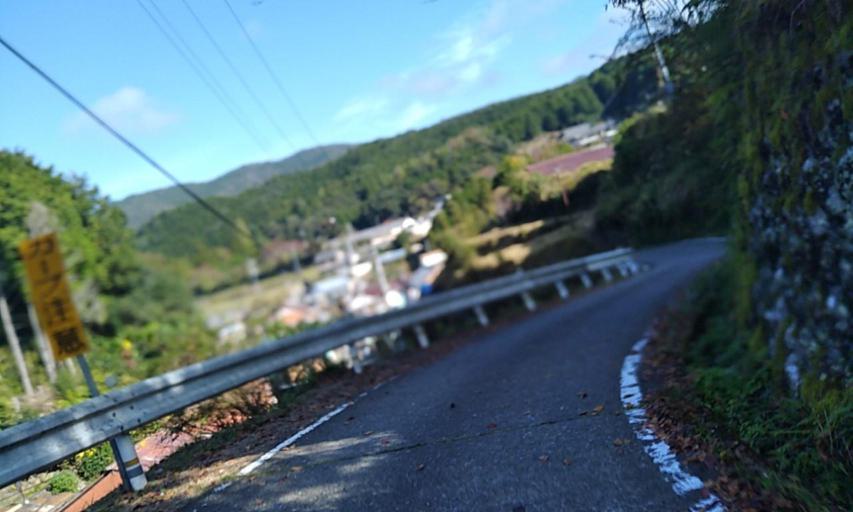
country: JP
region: Wakayama
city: Shingu
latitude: 33.9217
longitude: 135.9828
